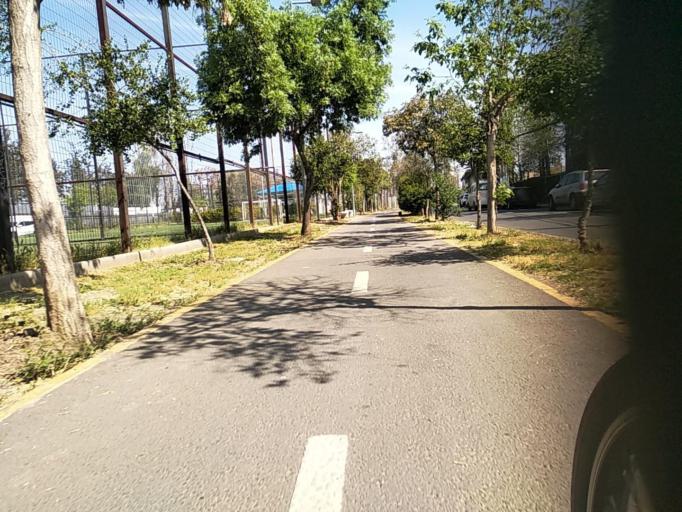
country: CL
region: Santiago Metropolitan
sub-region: Provincia de Santiago
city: Villa Presidente Frei, Nunoa, Santiago, Chile
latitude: -33.5025
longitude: -70.6062
